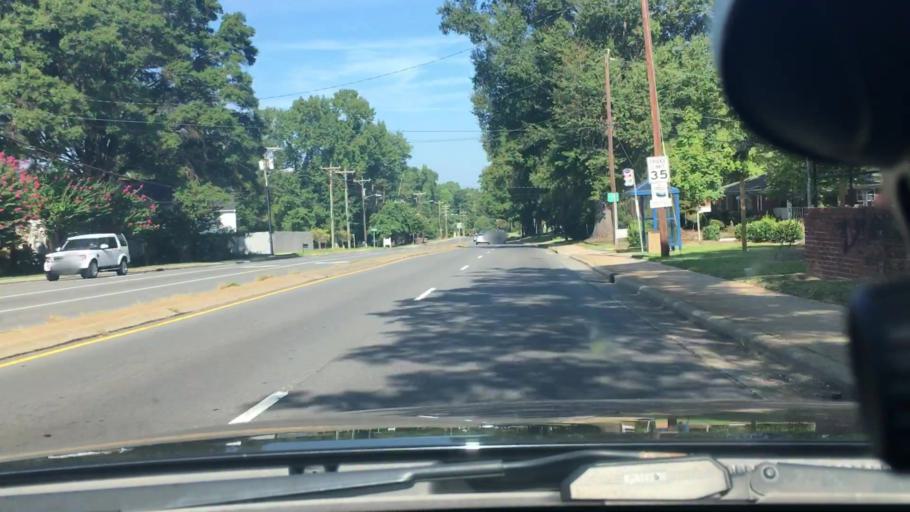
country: US
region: North Carolina
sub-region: Mecklenburg County
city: Matthews
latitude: 35.1863
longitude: -80.7309
